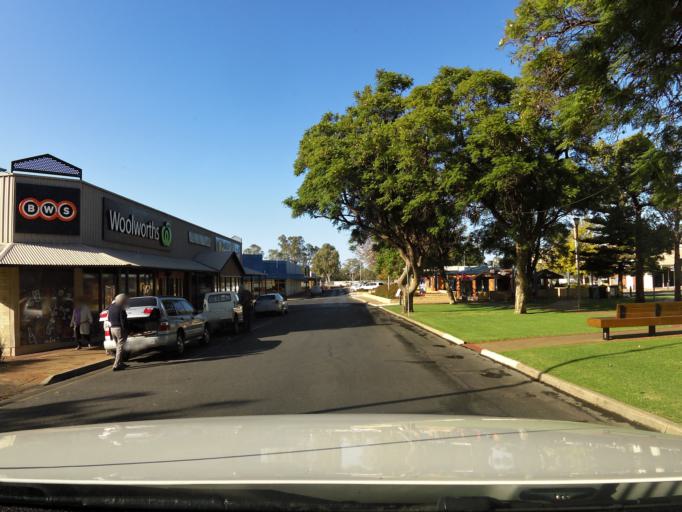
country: AU
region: South Australia
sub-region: Berri and Barmera
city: Berri
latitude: -34.2859
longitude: 140.6021
